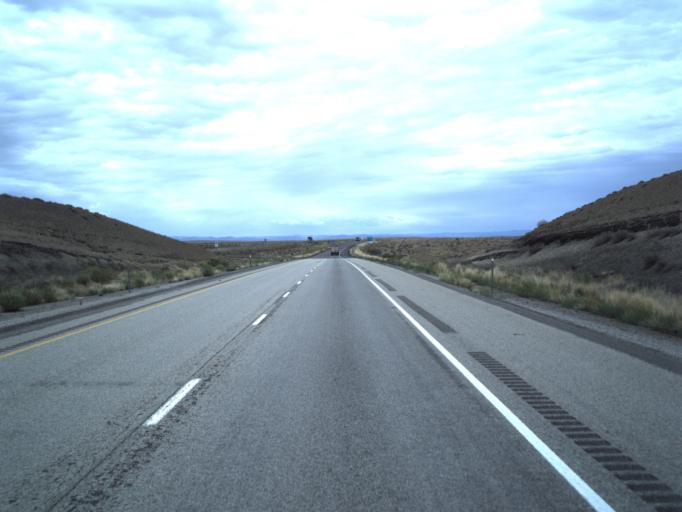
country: US
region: Colorado
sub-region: Mesa County
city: Loma
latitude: 39.0293
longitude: -109.2907
